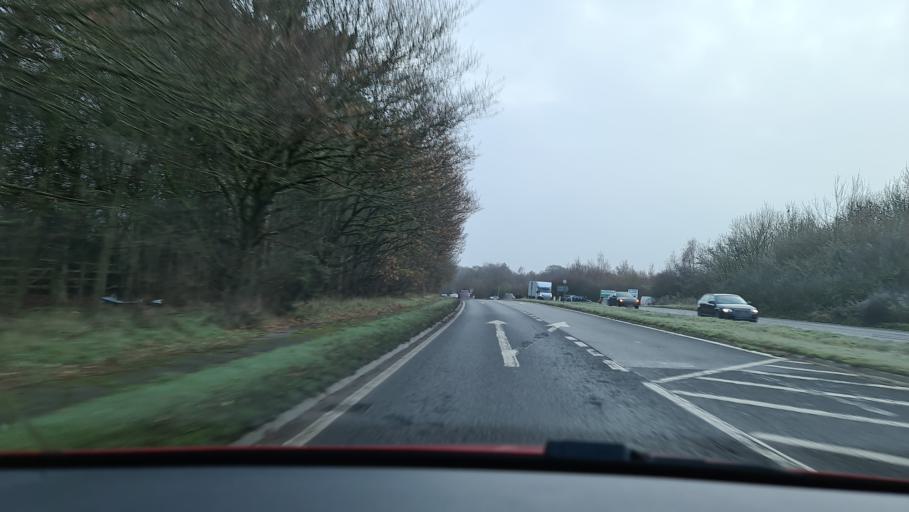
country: GB
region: England
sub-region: Buckinghamshire
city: Seer Green
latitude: 51.5988
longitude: -0.6166
